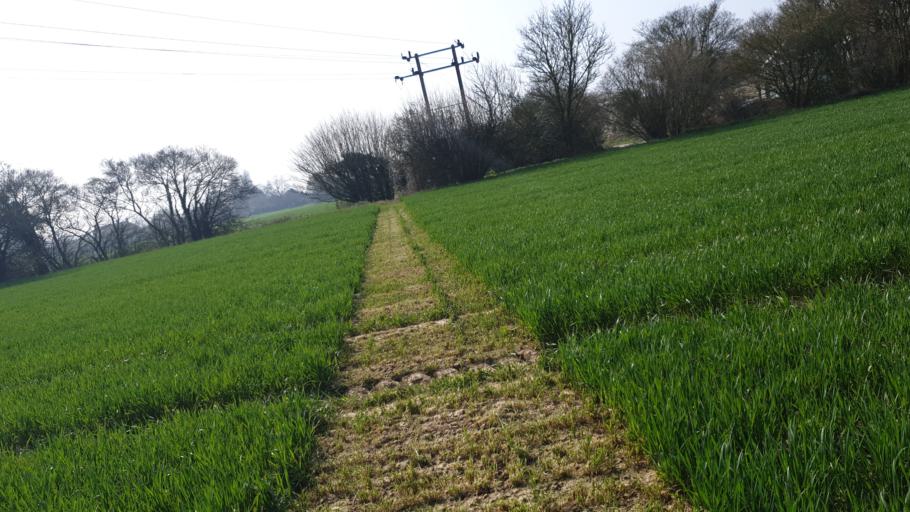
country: GB
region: England
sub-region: Essex
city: Mistley
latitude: 51.9201
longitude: 1.1486
